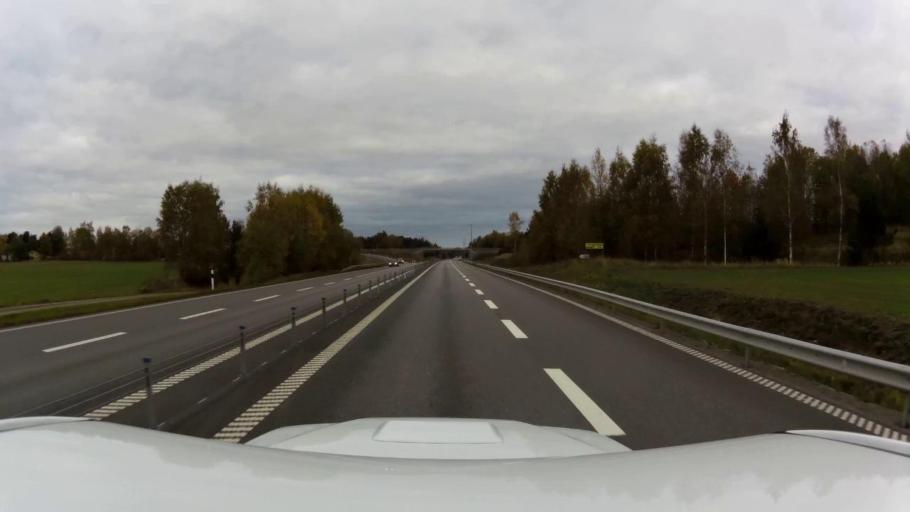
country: SE
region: OEstergoetland
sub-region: Linkopings Kommun
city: Ljungsbro
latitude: 58.4898
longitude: 15.4709
